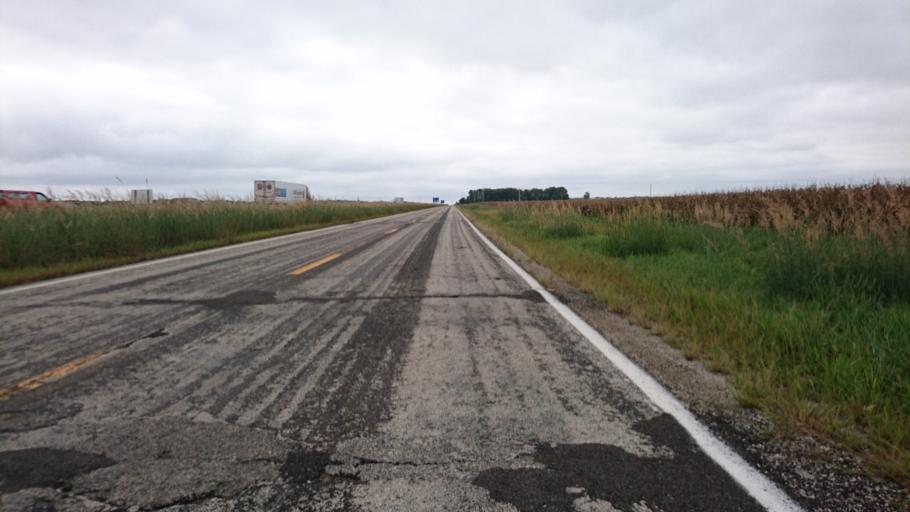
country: US
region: Illinois
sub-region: Montgomery County
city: Raymond
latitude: 39.3100
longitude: -89.6430
